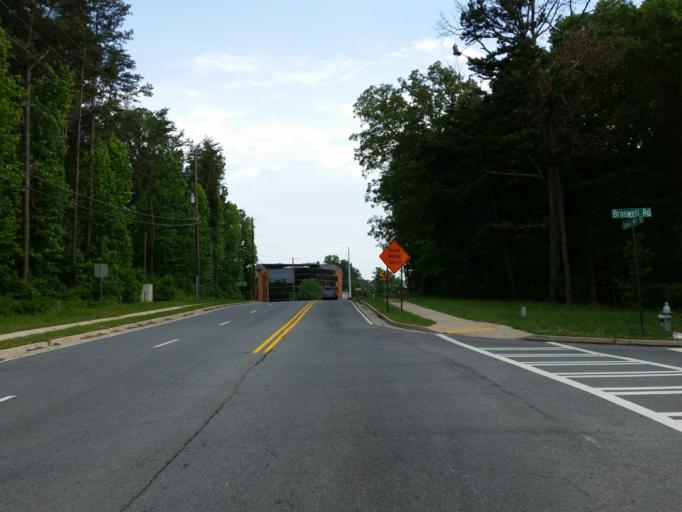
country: US
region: Georgia
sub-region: Cobb County
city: Marietta
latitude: 33.9766
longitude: -84.4849
